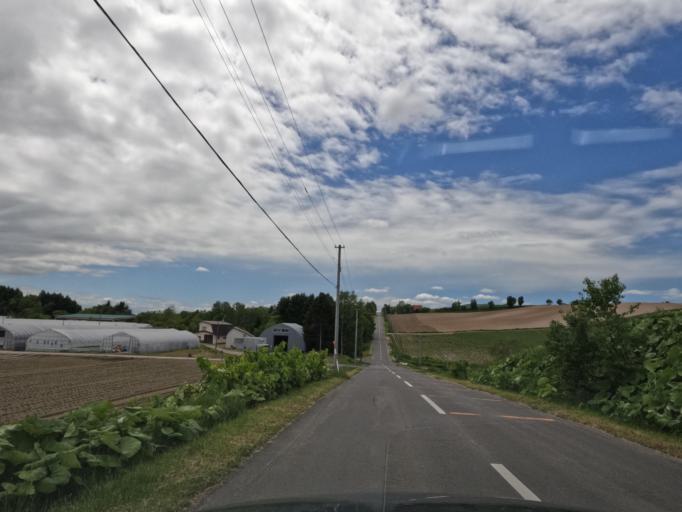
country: JP
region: Hokkaido
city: Shimo-furano
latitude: 43.5260
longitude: 142.4353
